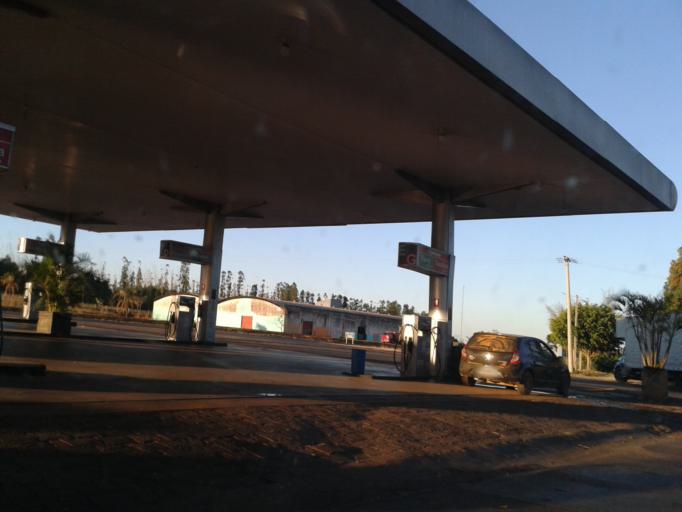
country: BR
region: Goias
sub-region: Goias
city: Goias
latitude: -16.0045
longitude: -50.0307
